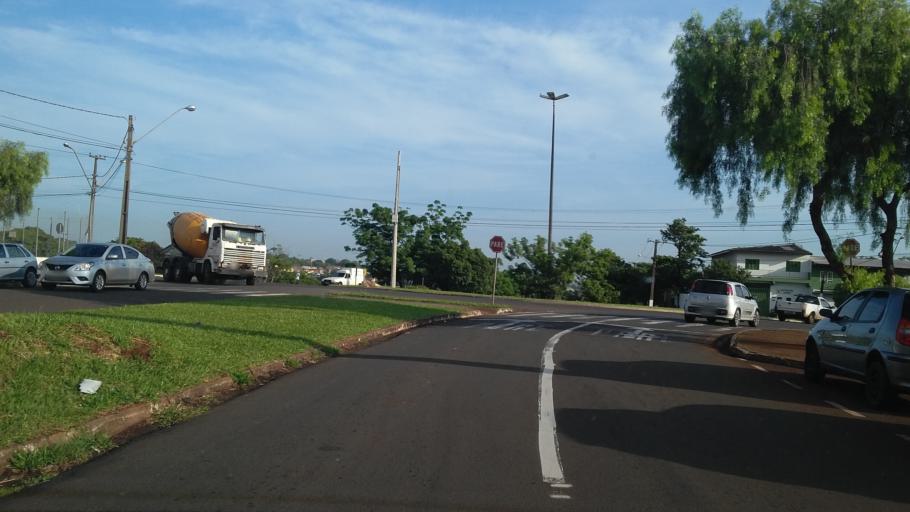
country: BR
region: Parana
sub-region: Londrina
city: Londrina
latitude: -23.2976
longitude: -51.1904
